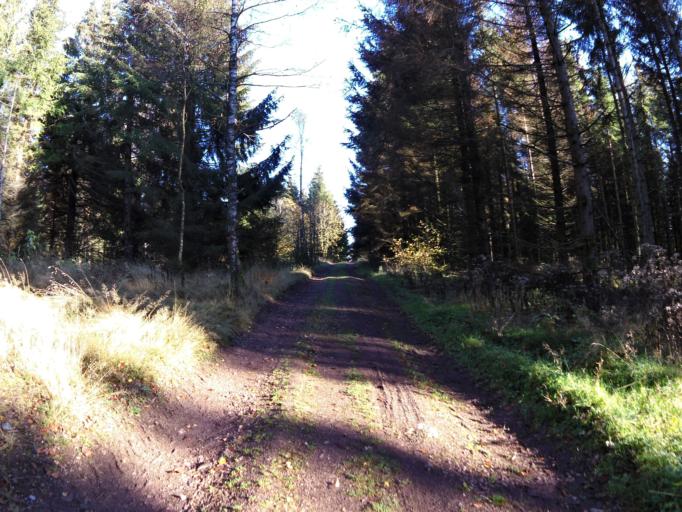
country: DE
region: Thuringia
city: Ruhla
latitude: 50.9054
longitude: 10.3536
